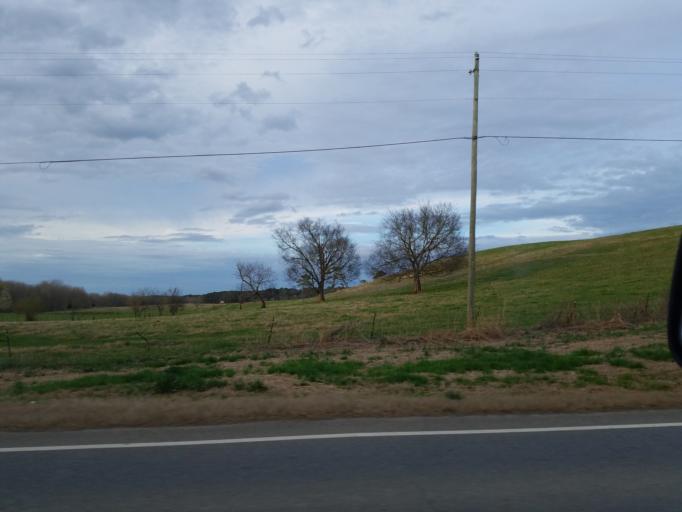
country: US
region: Georgia
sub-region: Bartow County
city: Rydal
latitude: 34.4345
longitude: -84.7124
